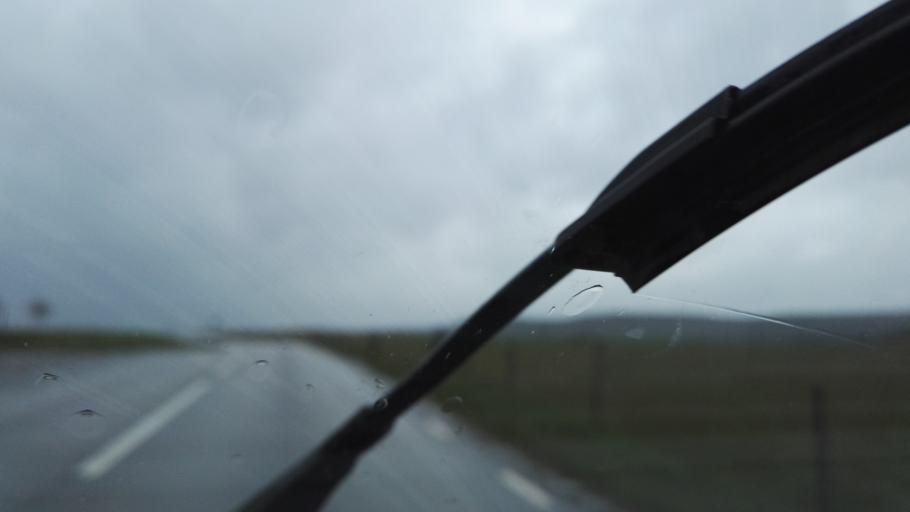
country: SE
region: Skane
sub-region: Simrishamns Kommun
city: Kivik
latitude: 55.7146
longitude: 14.1542
